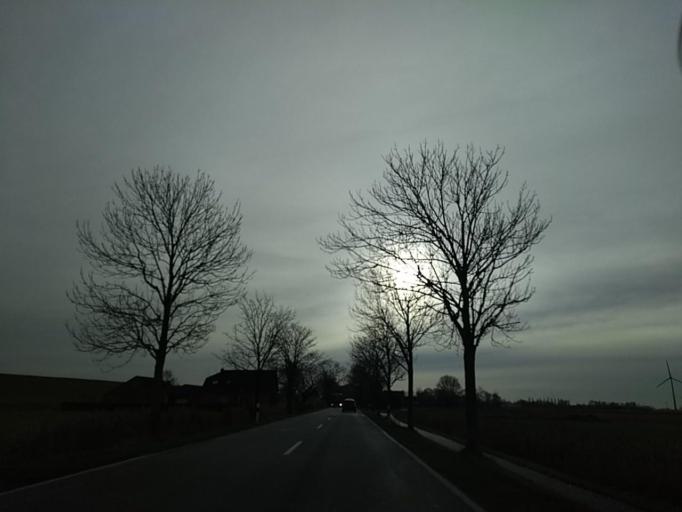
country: DE
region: Lower Saxony
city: Jemgum
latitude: 53.2430
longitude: 7.3913
